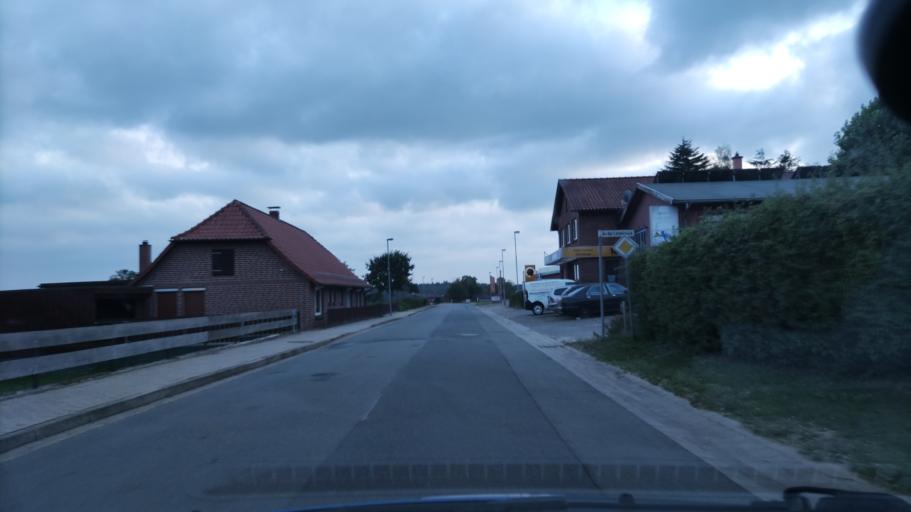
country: DE
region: Lower Saxony
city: Tosterglope
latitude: 53.2098
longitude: 10.8179
